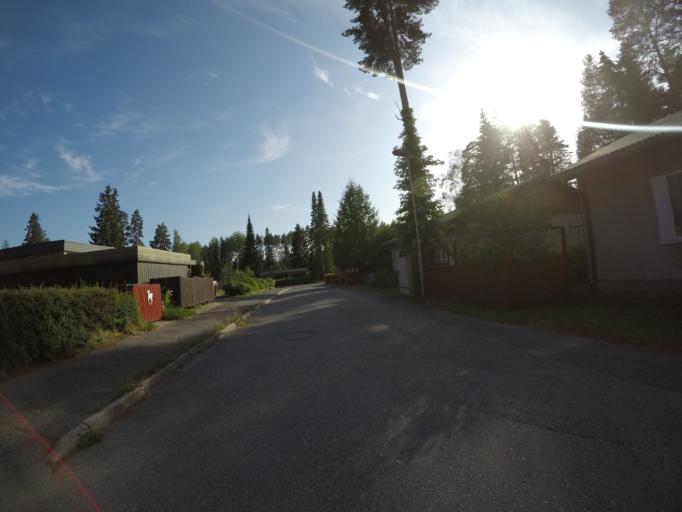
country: FI
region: Haeme
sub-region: Haemeenlinna
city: Haemeenlinna
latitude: 60.9753
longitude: 24.3928
